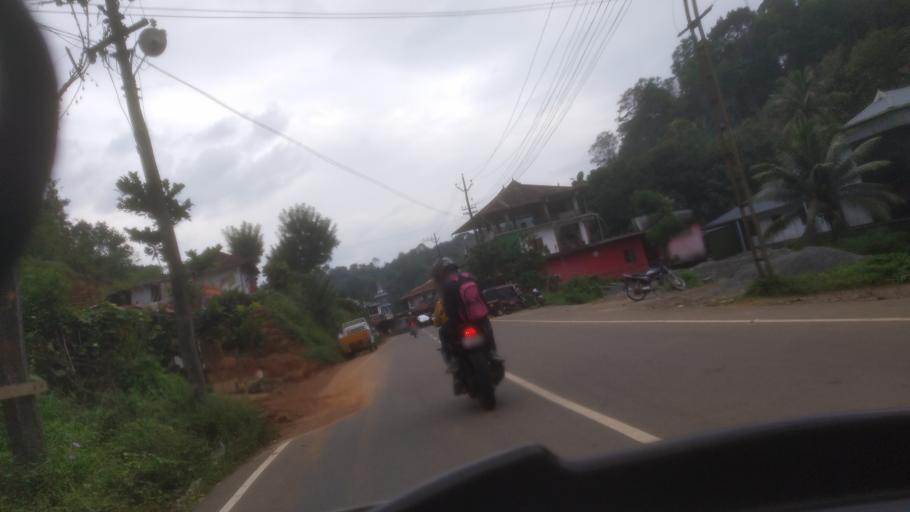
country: IN
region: Kerala
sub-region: Idukki
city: Idukki
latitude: 9.9467
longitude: 77.0144
